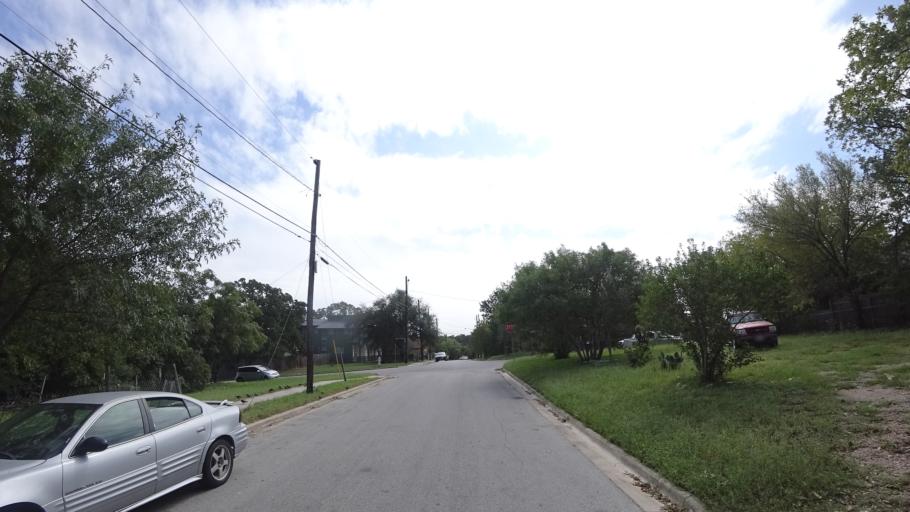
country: US
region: Texas
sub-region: Travis County
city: Austin
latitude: 30.2732
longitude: -97.7188
